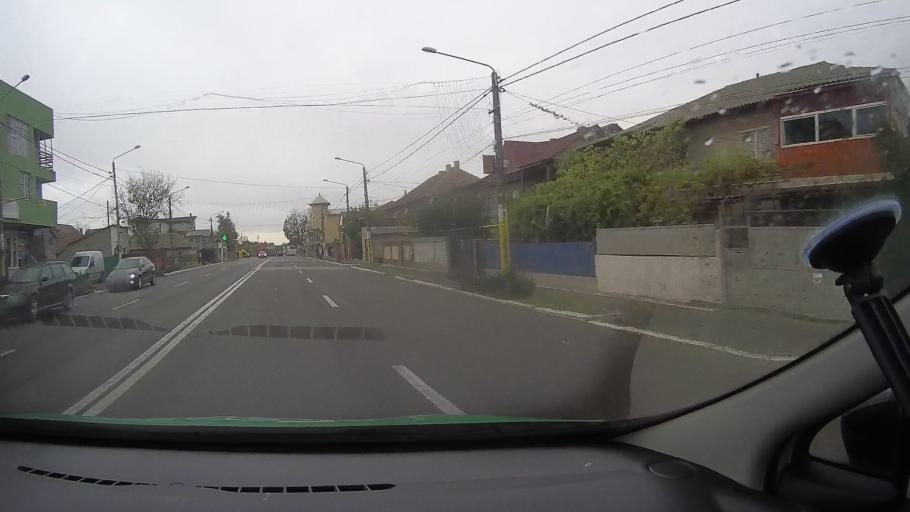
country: RO
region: Constanta
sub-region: Comuna Valu lui Traian
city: Valu lui Traian
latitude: 44.1649
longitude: 28.4855
